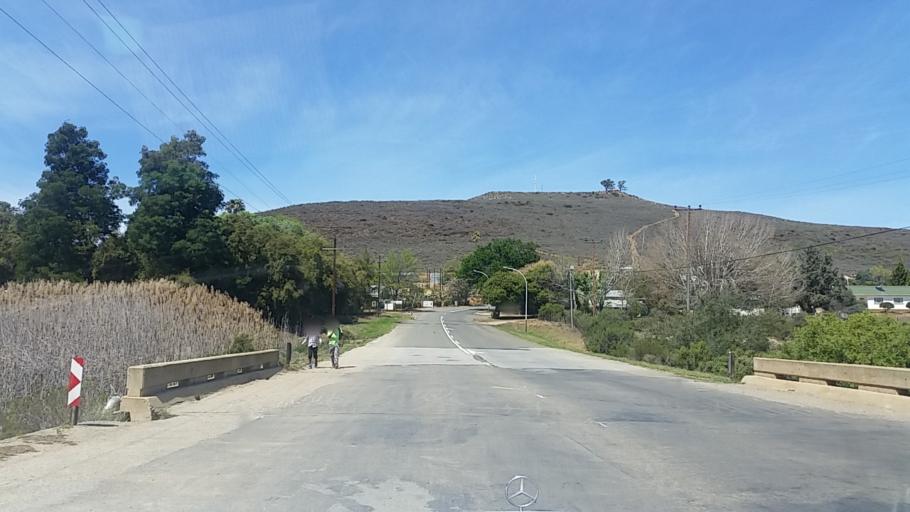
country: ZA
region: Western Cape
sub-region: Eden District Municipality
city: Knysna
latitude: -33.6536
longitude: 23.1348
